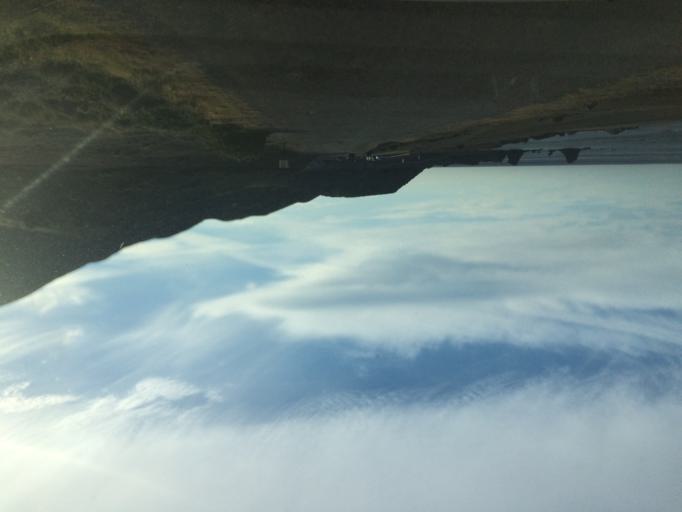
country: ES
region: Andalusia
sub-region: Provincia de Almeria
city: San Jose
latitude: 36.7975
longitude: -2.0634
